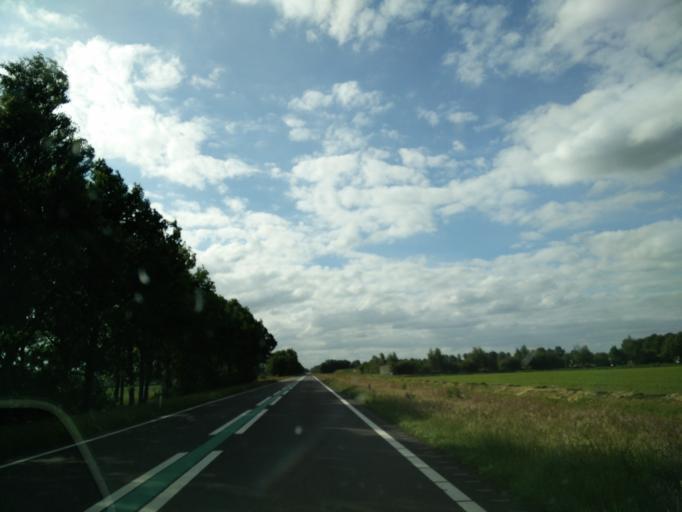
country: NL
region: Drenthe
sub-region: Gemeente Assen
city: Assen
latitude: 52.8429
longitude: 6.5819
